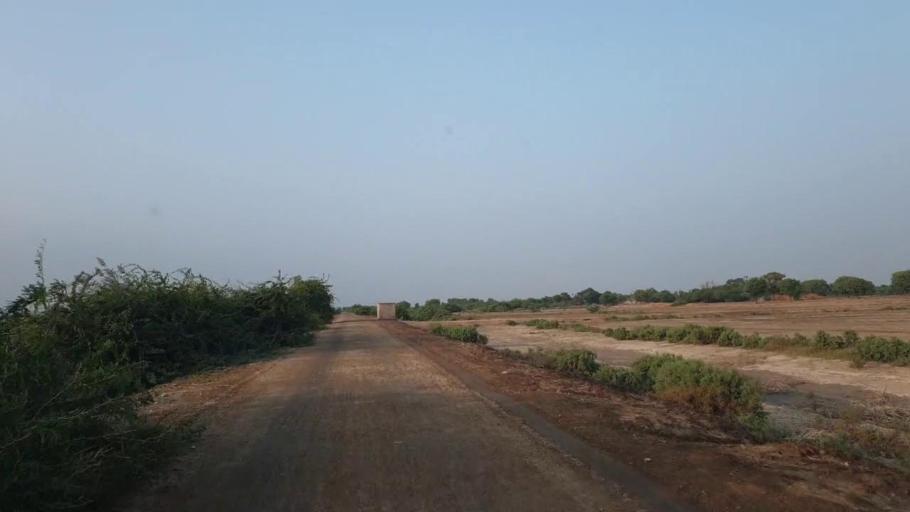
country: PK
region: Sindh
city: Tando Ghulam Ali
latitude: 25.0602
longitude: 68.9605
